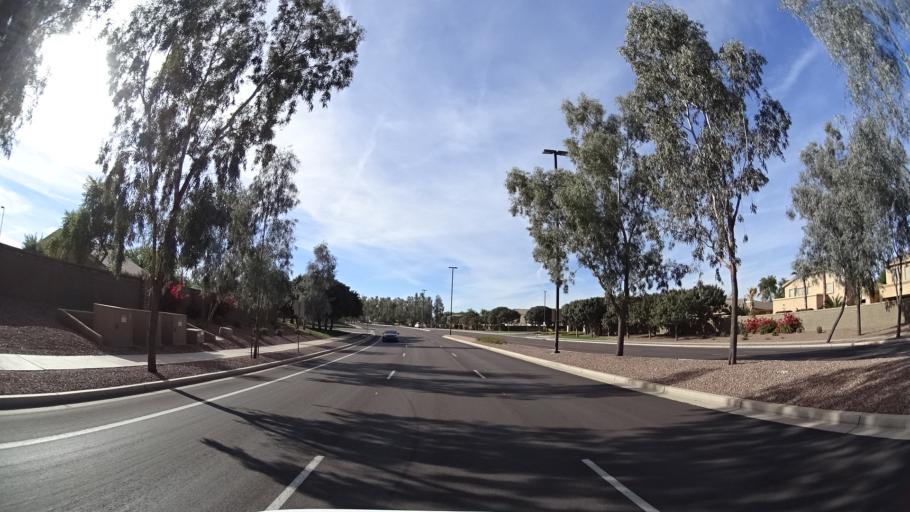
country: US
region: Arizona
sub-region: Maricopa County
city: Queen Creek
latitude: 33.2792
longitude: -111.6965
